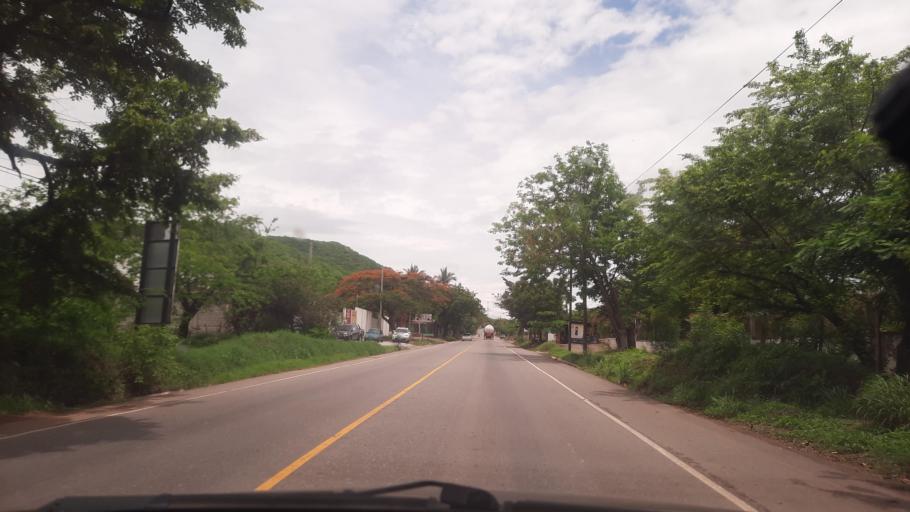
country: GT
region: Zacapa
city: Rio Hondo
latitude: 15.0796
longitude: -89.4883
